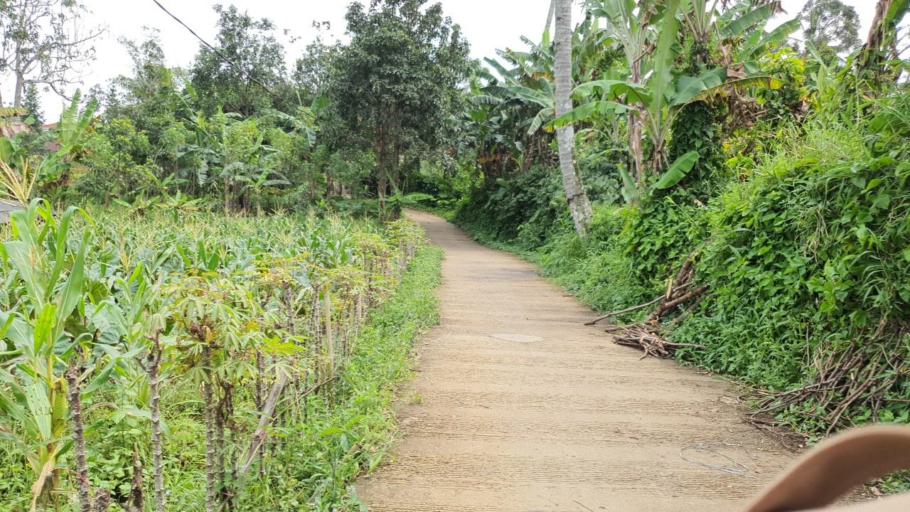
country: ID
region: West Java
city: Caringin
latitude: -6.6456
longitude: 106.8882
